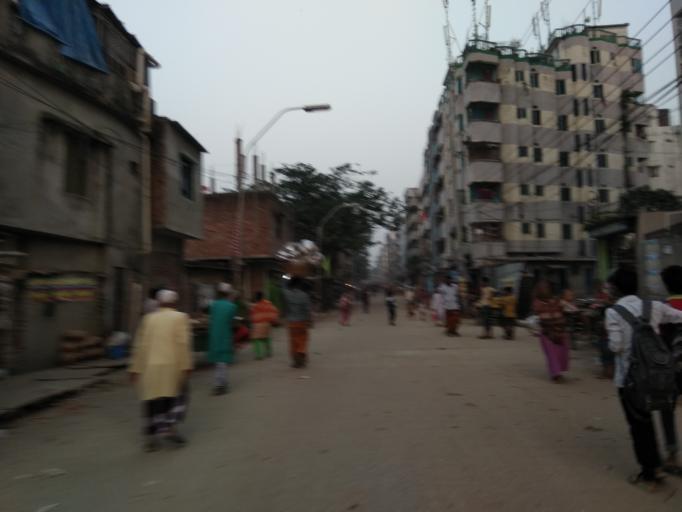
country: BD
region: Dhaka
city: Tungi
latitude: 23.8136
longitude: 90.3710
